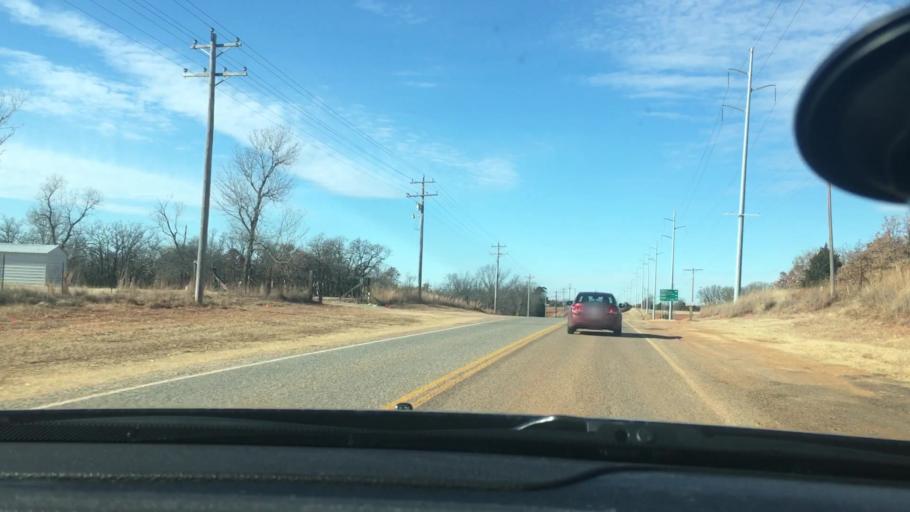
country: US
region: Oklahoma
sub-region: Cleveland County
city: Lexington
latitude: 35.0150
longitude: -97.1920
